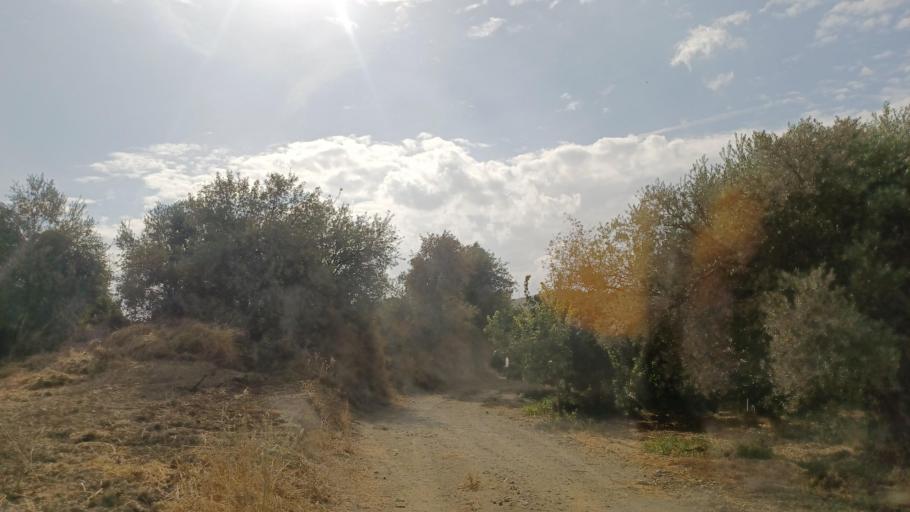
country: CY
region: Pafos
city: Polis
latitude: 35.0315
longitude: 32.4377
